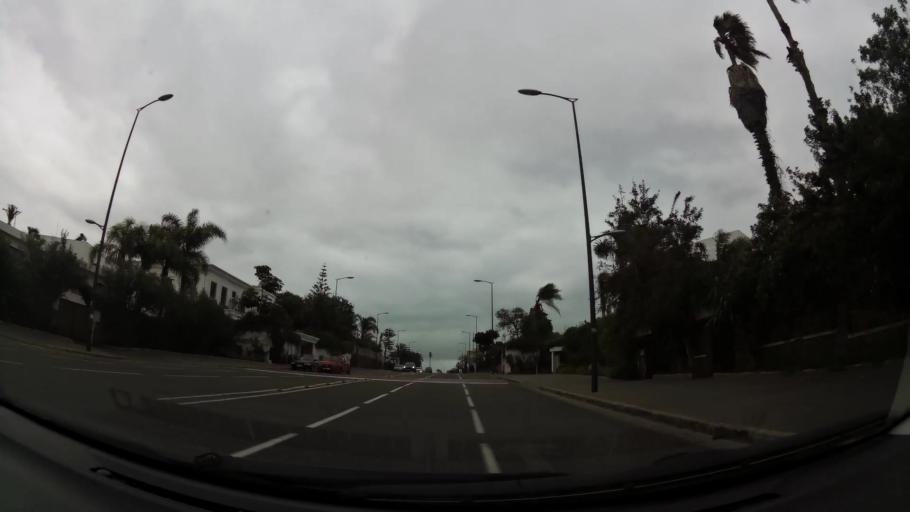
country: MA
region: Grand Casablanca
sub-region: Casablanca
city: Casablanca
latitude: 33.5925
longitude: -7.6595
